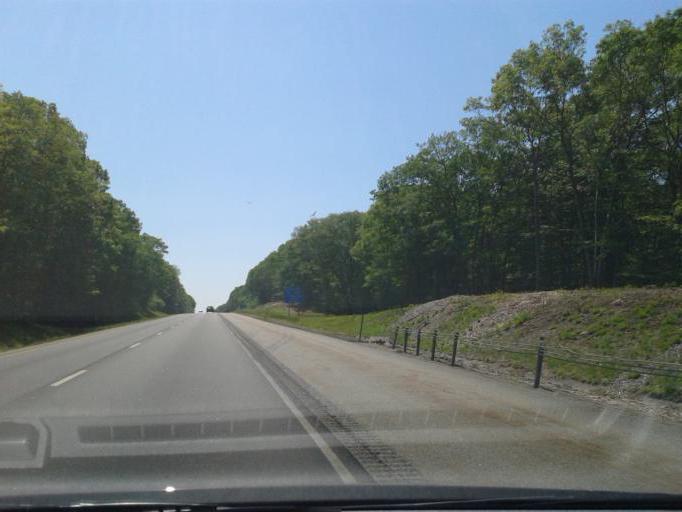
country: US
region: Rhode Island
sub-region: Washington County
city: Ashaway
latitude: 41.4256
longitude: -71.8306
